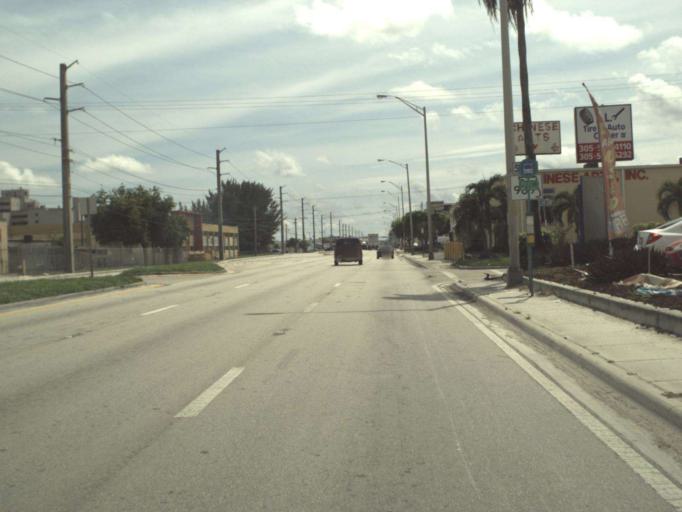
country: US
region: Florida
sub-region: Miami-Dade County
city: Virginia Gardens
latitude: 25.8147
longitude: -80.3135
